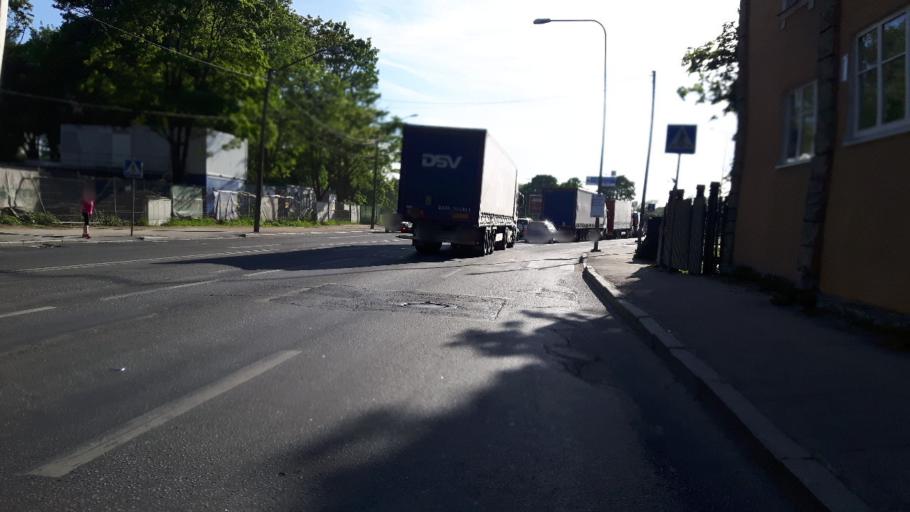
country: EE
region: Harju
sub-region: Tallinna linn
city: Tallinn
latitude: 59.4433
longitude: 24.7979
